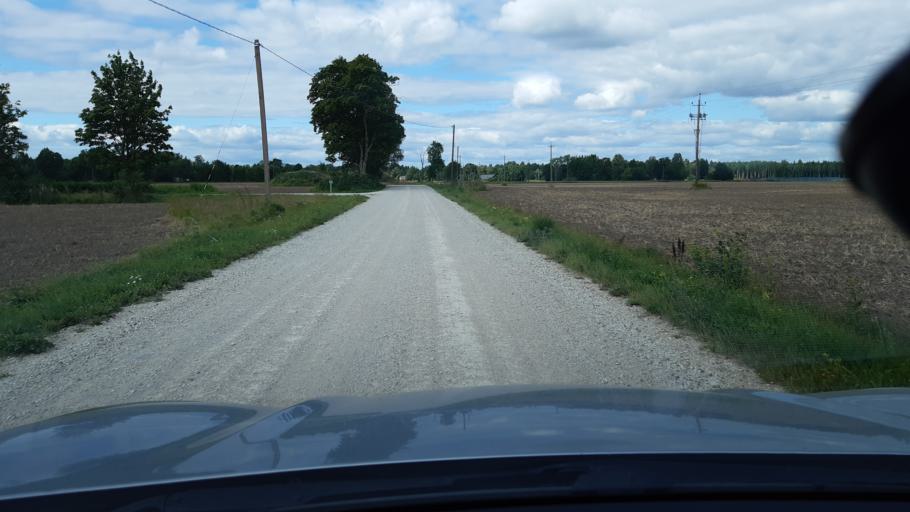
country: EE
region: Paernumaa
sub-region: Vaendra vald (alev)
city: Vandra
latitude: 58.7914
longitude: 25.0136
